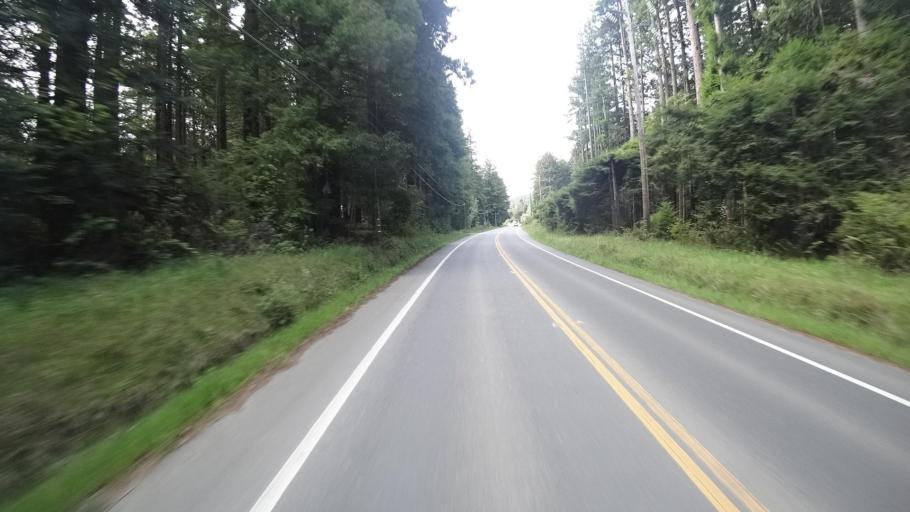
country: US
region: California
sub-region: Humboldt County
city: Myrtletown
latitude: 40.7762
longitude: -124.0735
